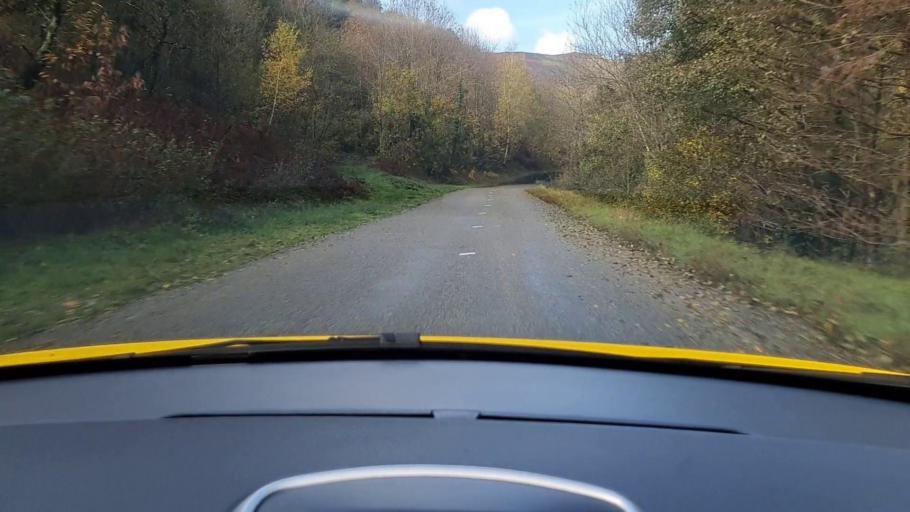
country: FR
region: Languedoc-Roussillon
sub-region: Departement du Gard
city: Valleraugue
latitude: 44.1691
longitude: 3.6503
